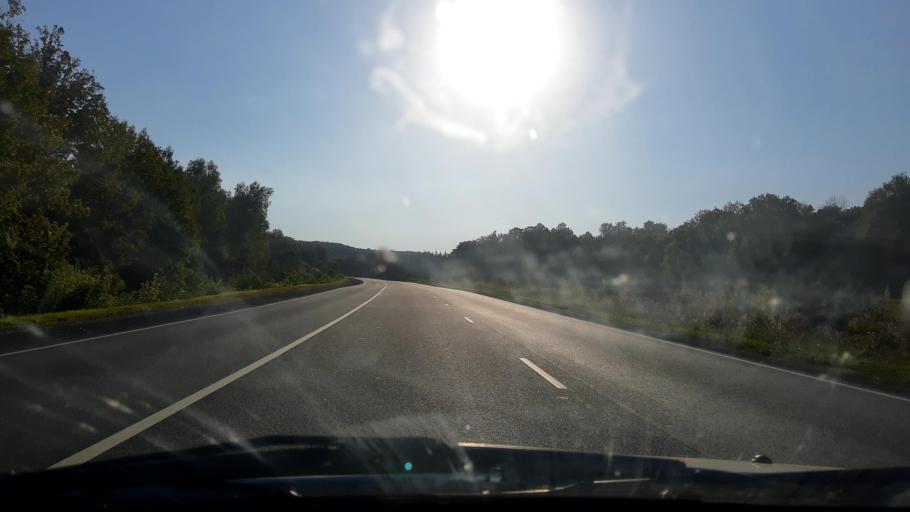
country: RU
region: Bashkortostan
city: Oktyabr'skiy
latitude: 54.4321
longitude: 53.4782
